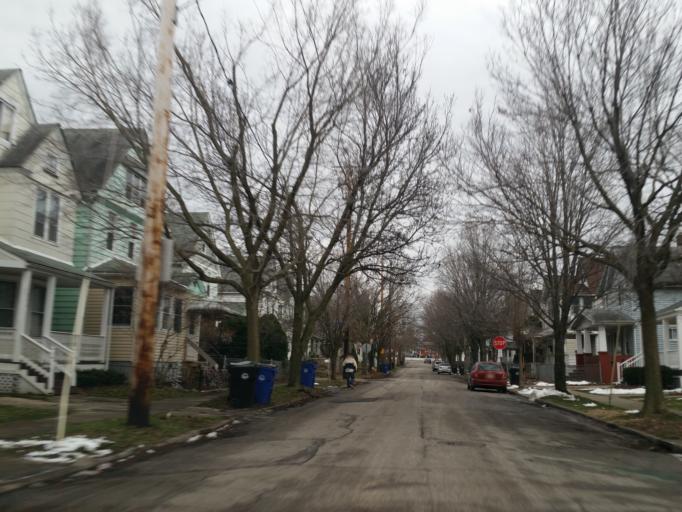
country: US
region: Ohio
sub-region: Cuyahoga County
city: Cleveland
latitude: 41.4847
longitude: -81.7376
